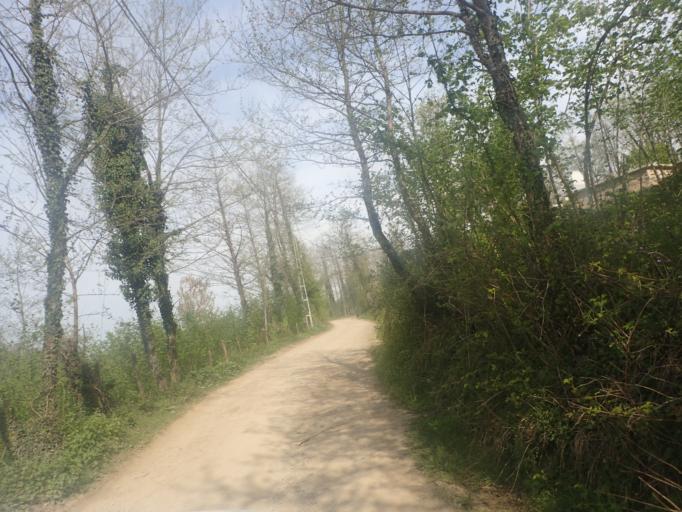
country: TR
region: Ordu
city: Catalpinar
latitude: 40.8817
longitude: 37.4885
